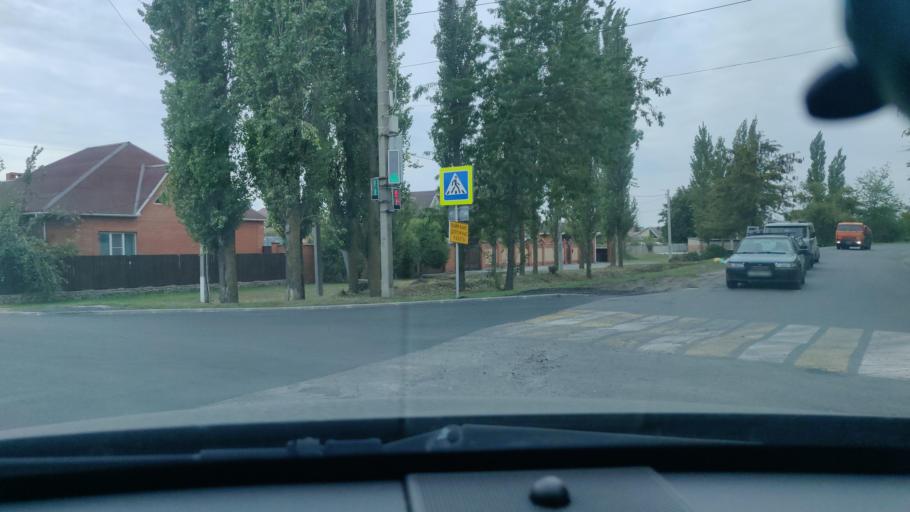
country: RU
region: Rostov
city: Ust'-Donetskiy
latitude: 47.6463
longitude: 40.8731
